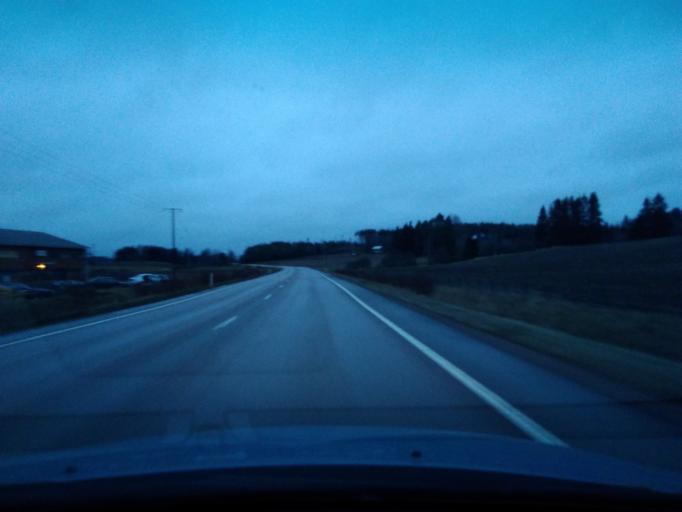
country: FI
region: Uusimaa
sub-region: Porvoo
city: Askola
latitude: 60.4614
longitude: 25.5785
